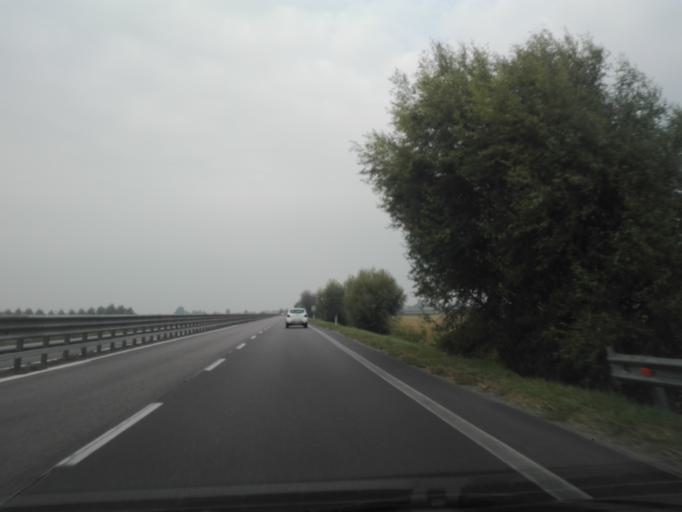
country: IT
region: Veneto
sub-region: Provincia di Verona
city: Villa Bartolomea
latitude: 45.1532
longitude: 11.3307
